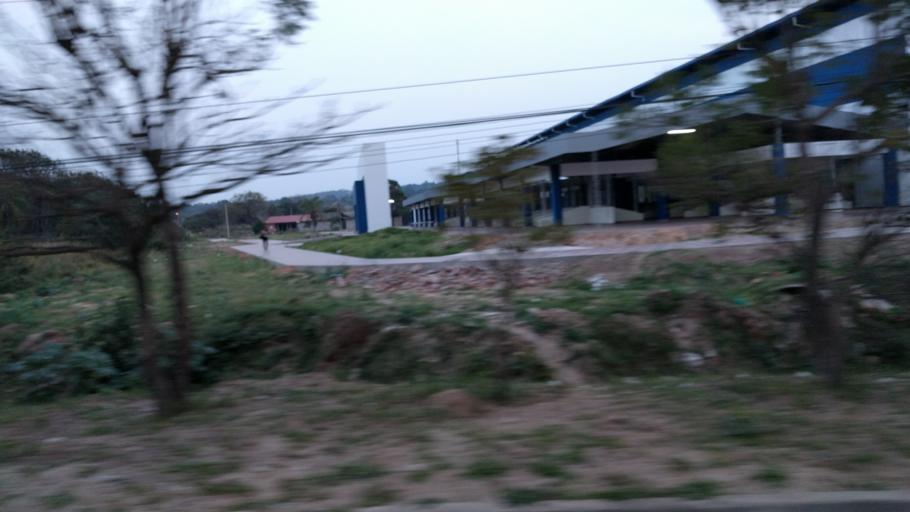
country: BO
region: Santa Cruz
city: Santa Rita
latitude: -17.8912
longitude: -63.3185
